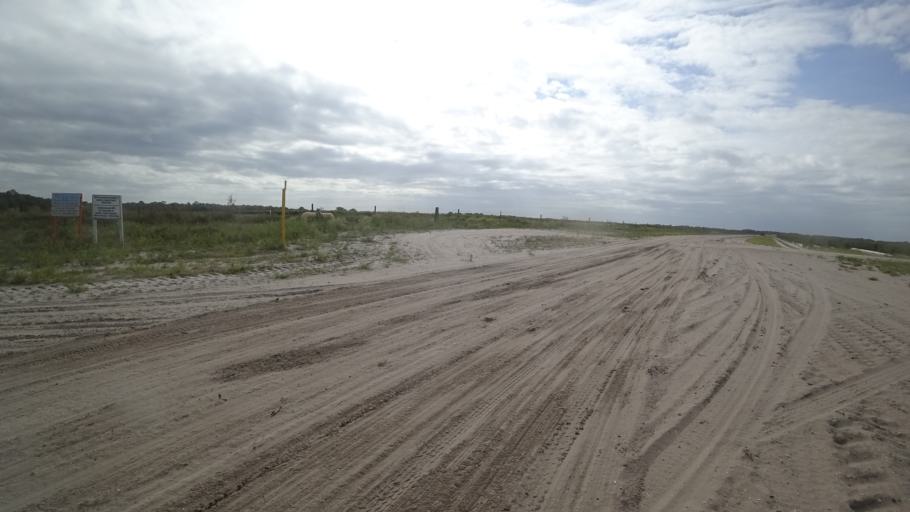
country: US
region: Florida
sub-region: Hillsborough County
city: Wimauma
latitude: 27.5925
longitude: -82.3112
